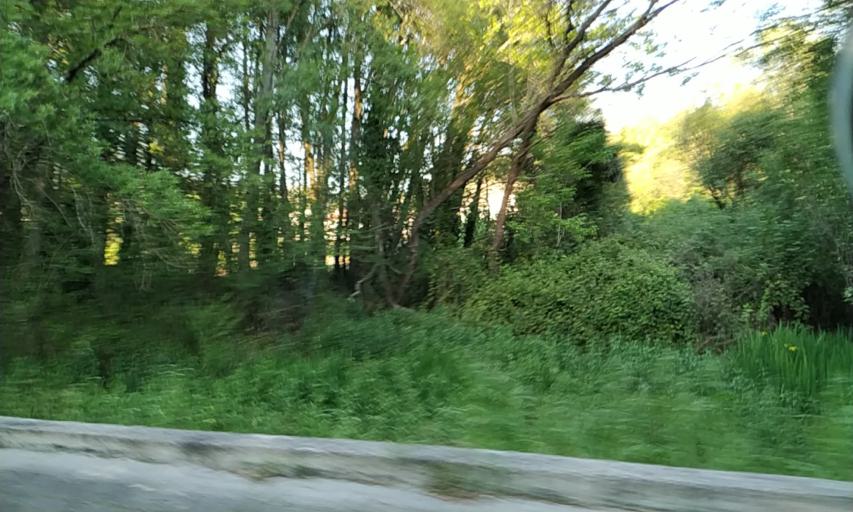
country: PT
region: Portalegre
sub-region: Marvao
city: Marvao
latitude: 39.3809
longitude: -7.3880
